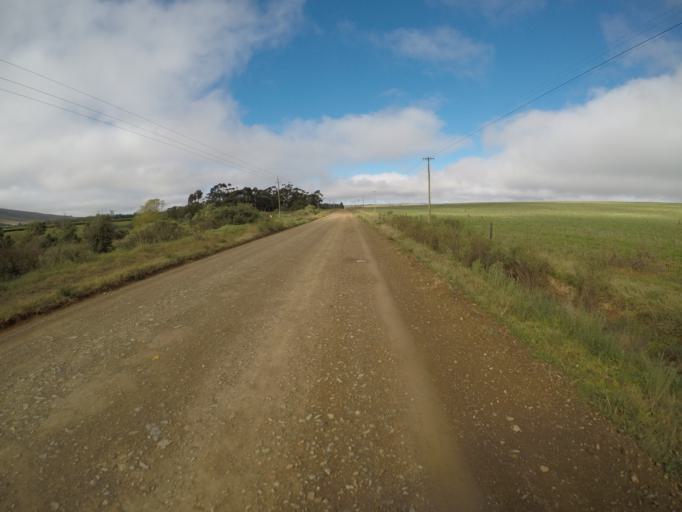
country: ZA
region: Western Cape
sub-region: Cape Winelands District Municipality
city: Ashton
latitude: -34.1367
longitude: 19.8591
